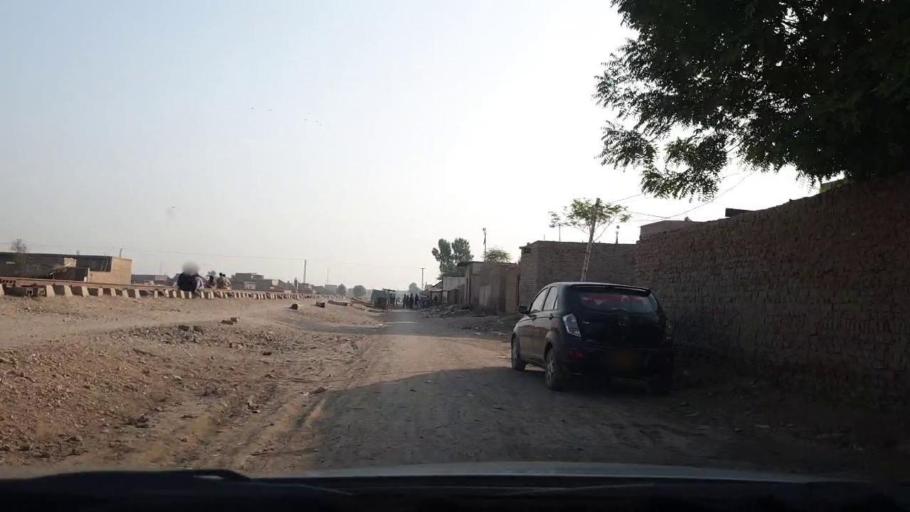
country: PK
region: Sindh
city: Larkana
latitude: 27.5327
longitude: 68.2017
